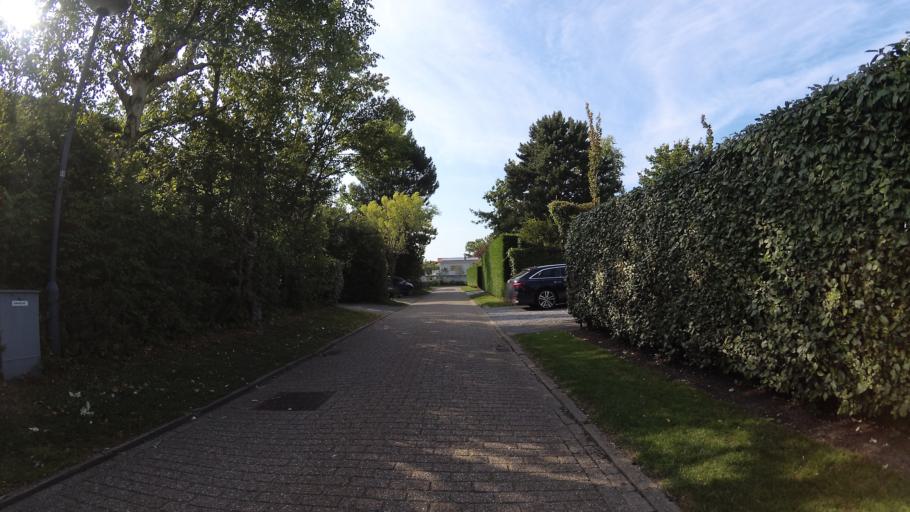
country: NL
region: Zeeland
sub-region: Gemeente Veere
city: Veere
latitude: 51.5638
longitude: 3.6746
